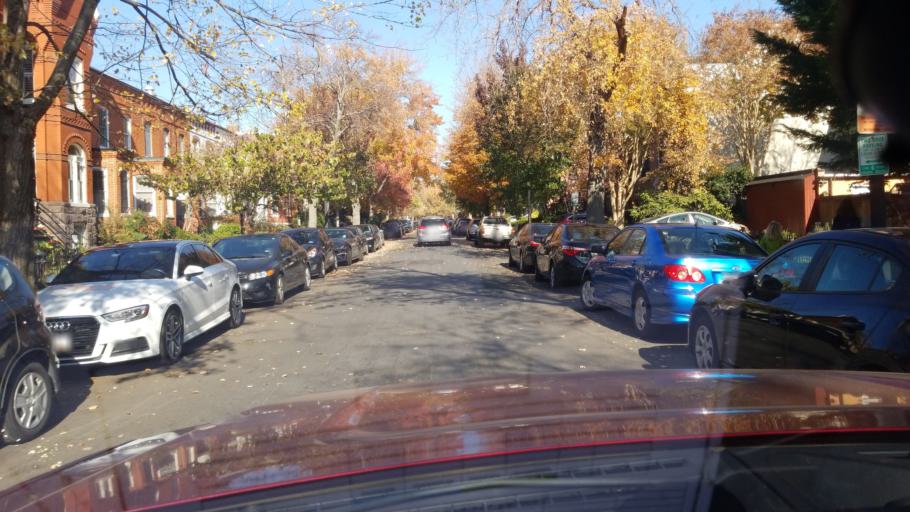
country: US
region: Washington, D.C.
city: Washington, D.C.
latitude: 38.8848
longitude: -76.9938
